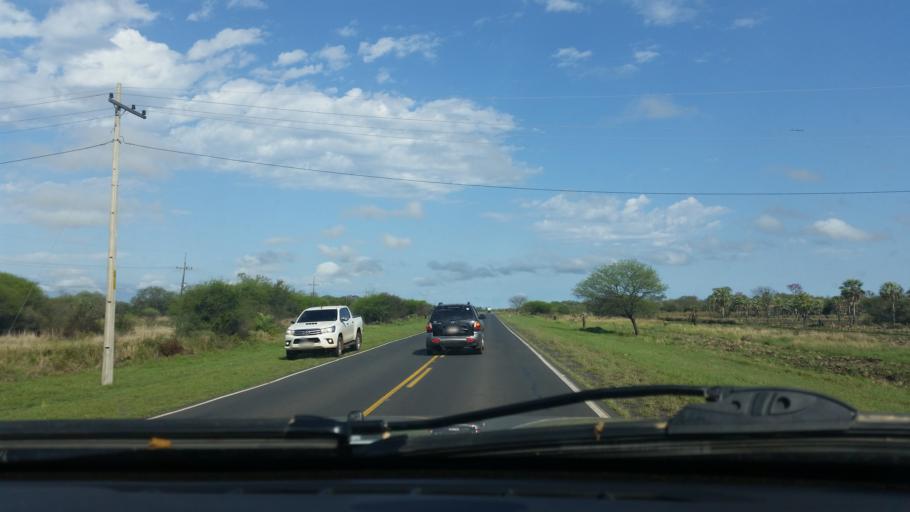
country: PY
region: Presidente Hayes
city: Benjamin Aceval
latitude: -24.9221
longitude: -57.5780
